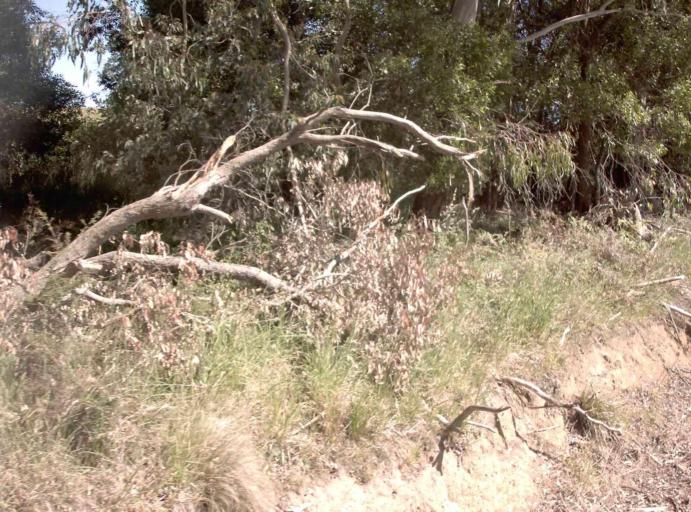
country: AU
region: New South Wales
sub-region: Bombala
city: Bombala
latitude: -37.1817
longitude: 148.7243
